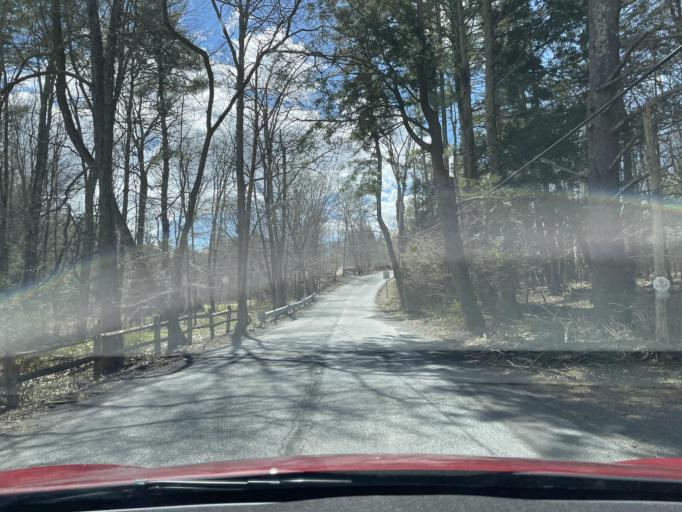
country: US
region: New York
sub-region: Ulster County
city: Zena
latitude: 42.0311
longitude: -74.0857
